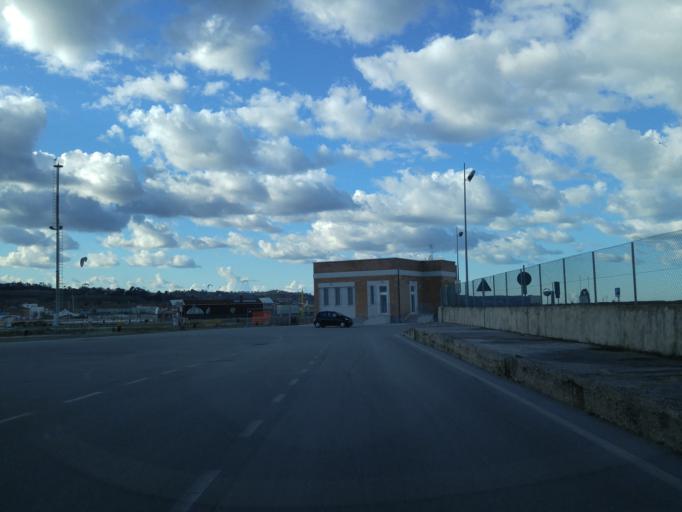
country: IT
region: The Marches
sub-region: Provincia di Pesaro e Urbino
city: Fano
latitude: 43.8521
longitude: 13.0172
